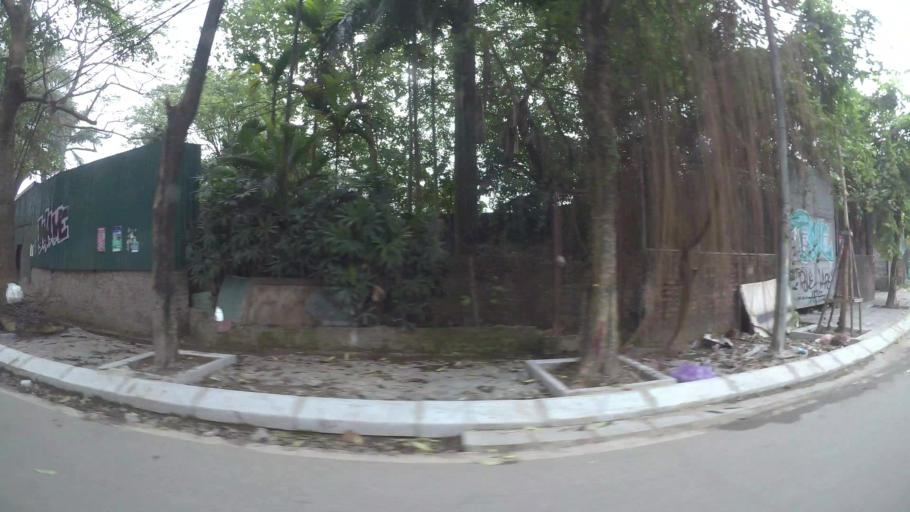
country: VN
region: Ha Noi
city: Tay Ho
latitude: 21.0627
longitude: 105.8211
